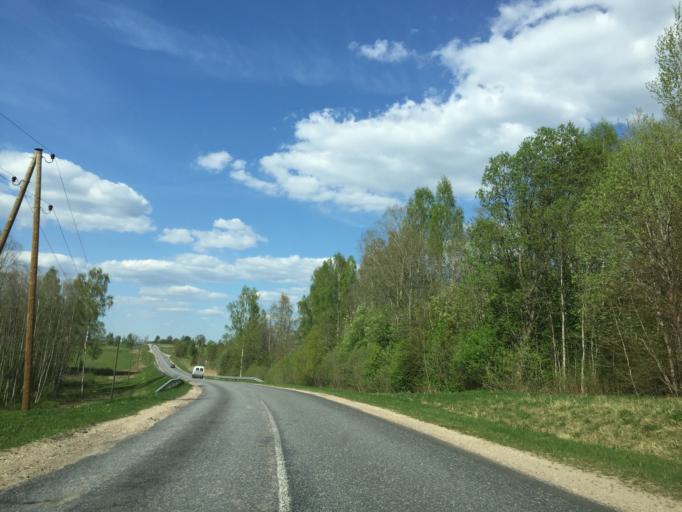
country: LV
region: Limbazu Rajons
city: Limbazi
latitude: 57.4433
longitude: 24.7237
